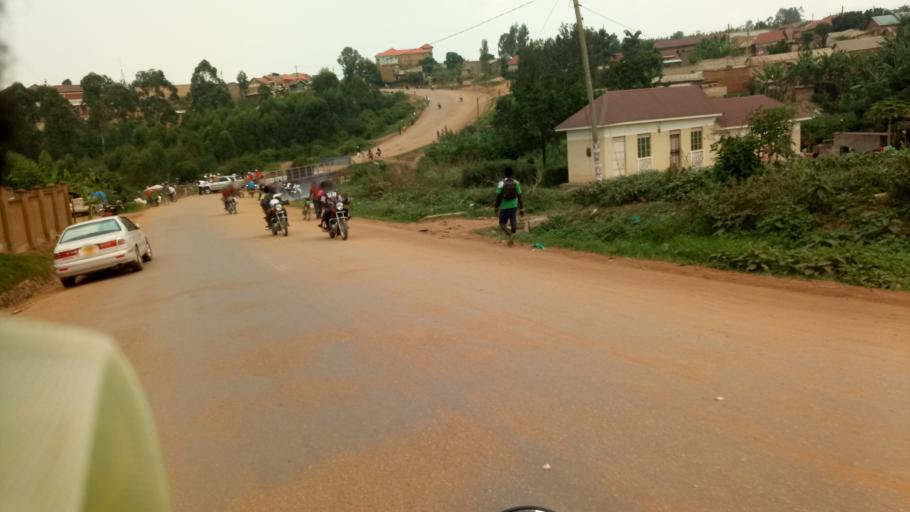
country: UG
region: Western Region
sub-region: Mbarara District
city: Mbarara
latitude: -0.6161
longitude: 30.6677
